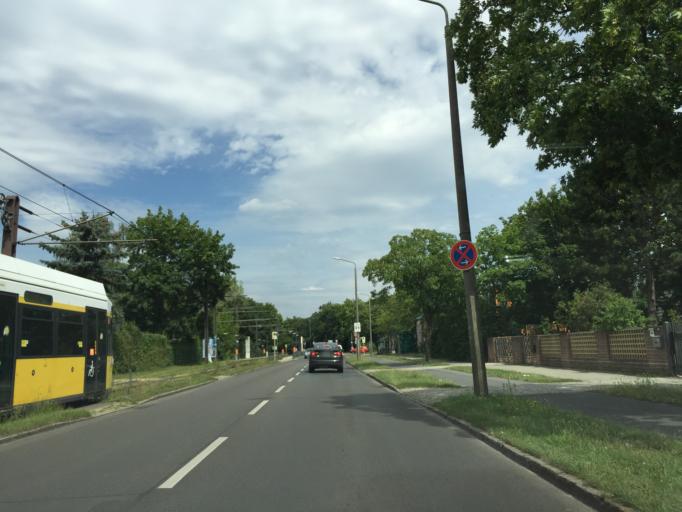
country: DE
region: Berlin
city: Mahlsdorf
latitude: 52.4974
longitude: 13.6124
